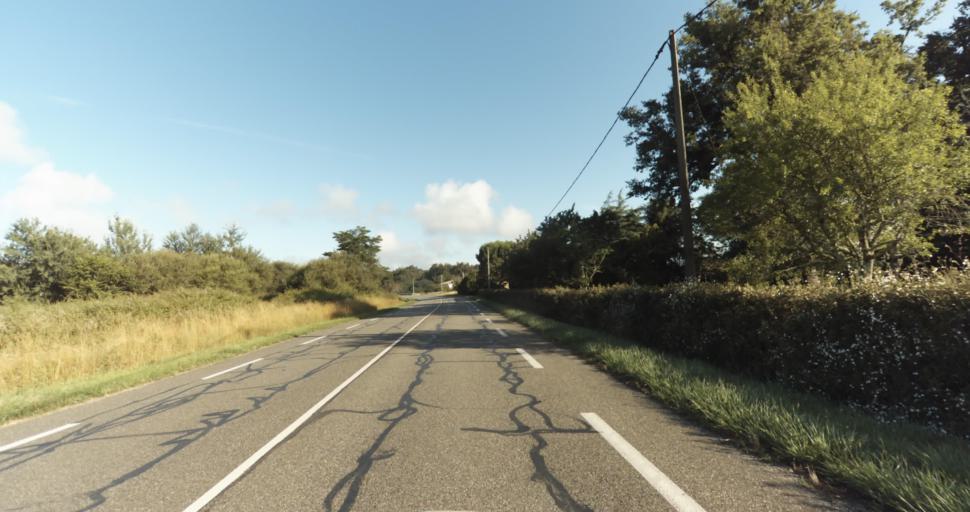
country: FR
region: Aquitaine
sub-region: Departement de la Gironde
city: Bazas
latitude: 44.4536
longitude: -0.2495
